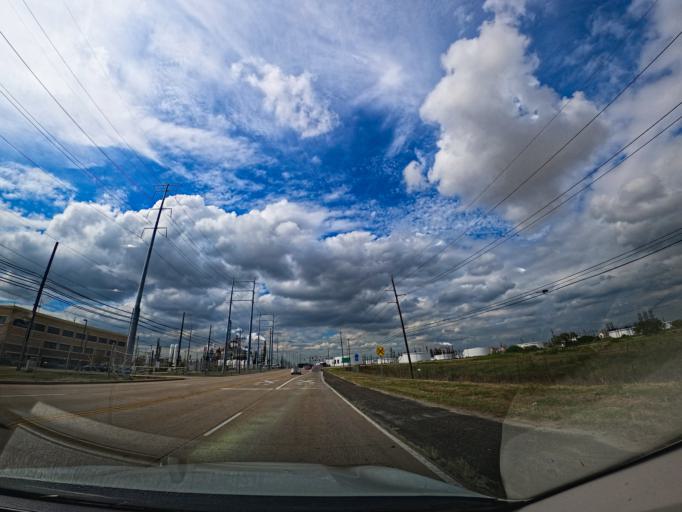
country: US
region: Texas
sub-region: Jefferson County
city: Port Arthur
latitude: 29.8654
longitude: -93.9616
